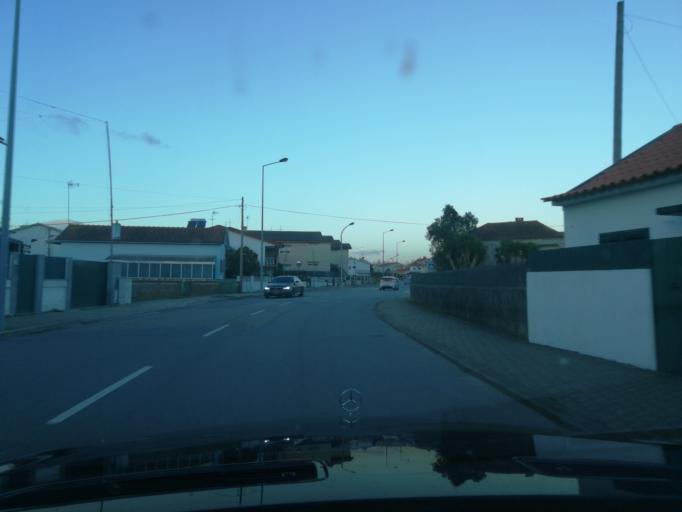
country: PT
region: Aveiro
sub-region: Estarreja
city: Estarreja
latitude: 40.7585
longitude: -8.5739
